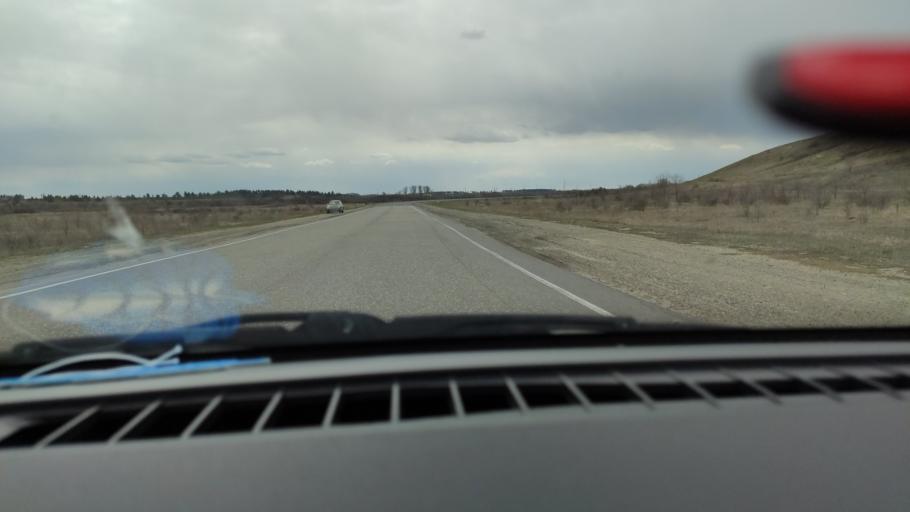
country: RU
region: Saratov
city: Sennoy
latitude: 52.0912
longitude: 46.8104
